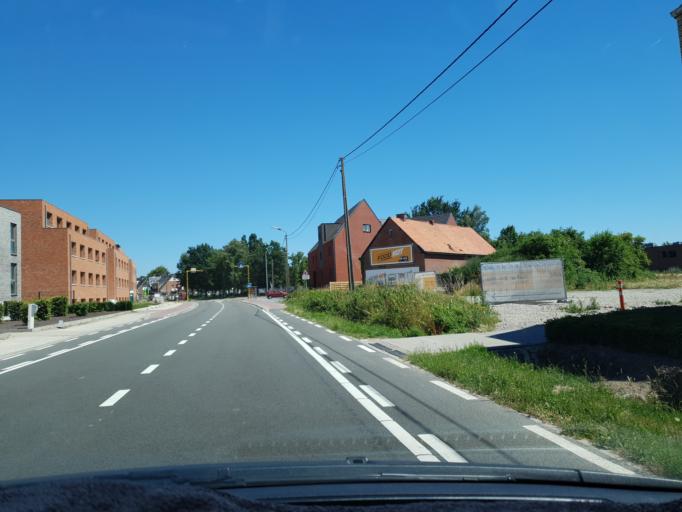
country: BE
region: Flanders
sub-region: Provincie Antwerpen
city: Geel
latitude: 51.1642
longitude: 4.9600
